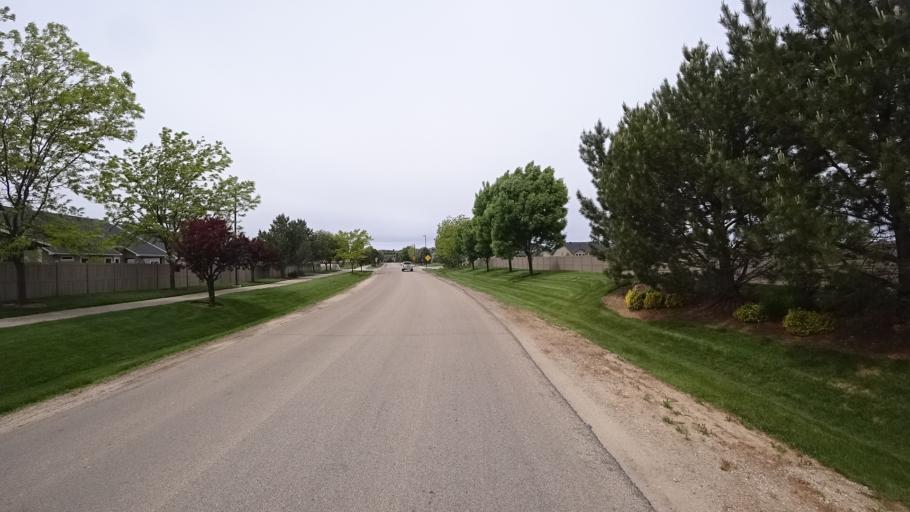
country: US
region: Idaho
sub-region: Ada County
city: Meridian
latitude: 43.5537
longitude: -116.3579
